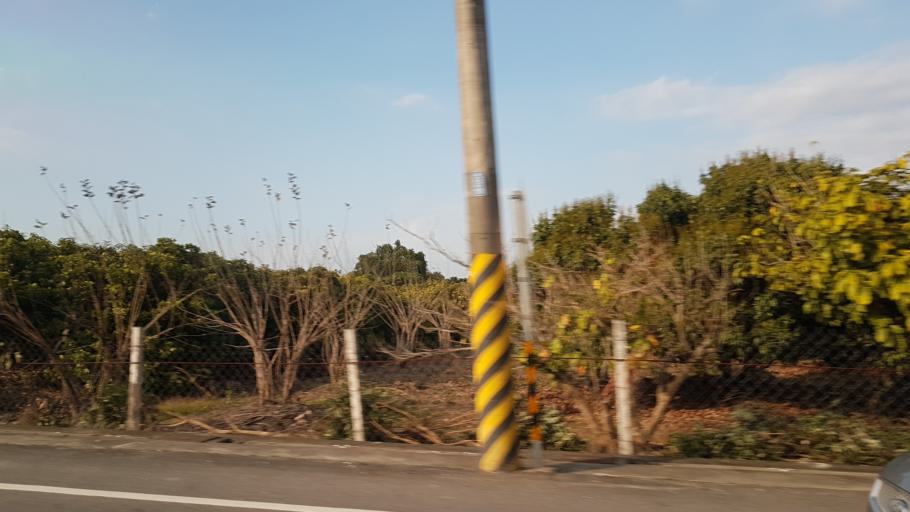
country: TW
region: Taiwan
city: Xinying
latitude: 23.3466
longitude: 120.4219
